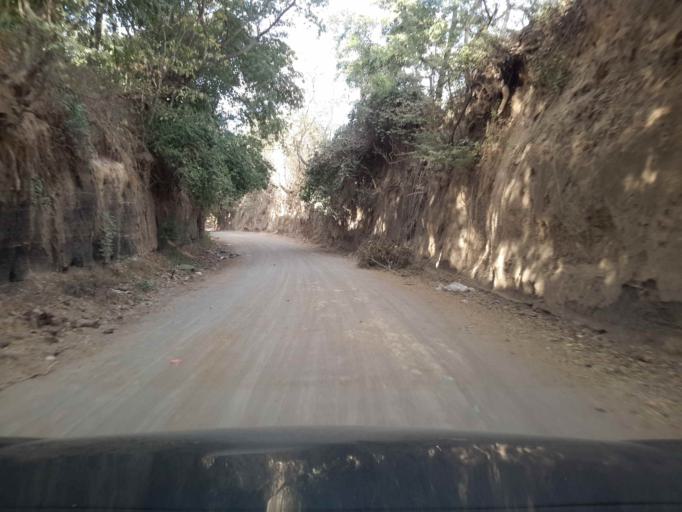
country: NI
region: Managua
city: Managua
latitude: 12.0882
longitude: -86.2620
